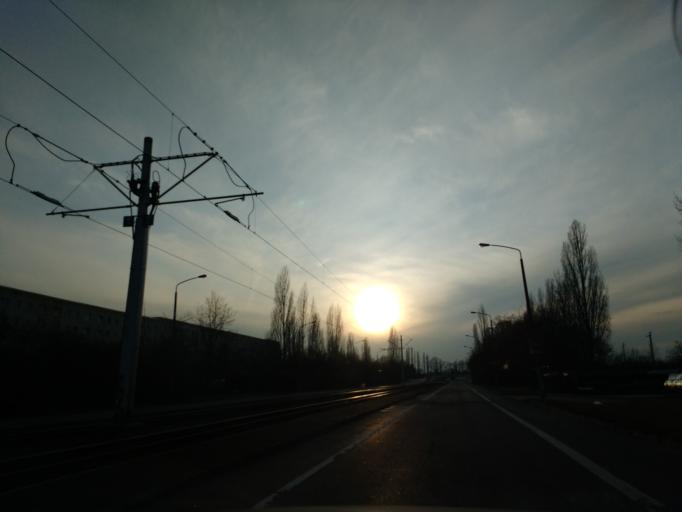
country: DE
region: Saxony-Anhalt
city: Schkopau
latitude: 51.4451
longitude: 11.9649
